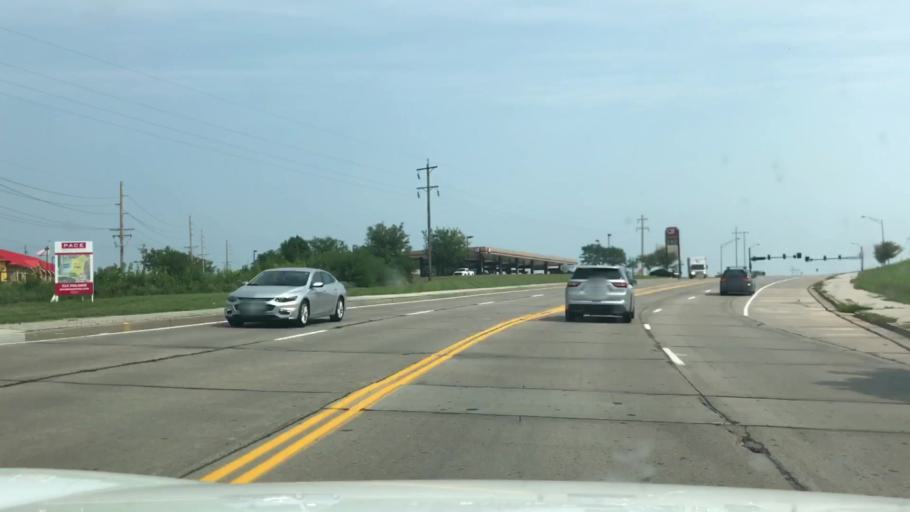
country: US
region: Missouri
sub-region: Saint Charles County
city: Dardenne Prairie
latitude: 38.7984
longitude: -90.7358
